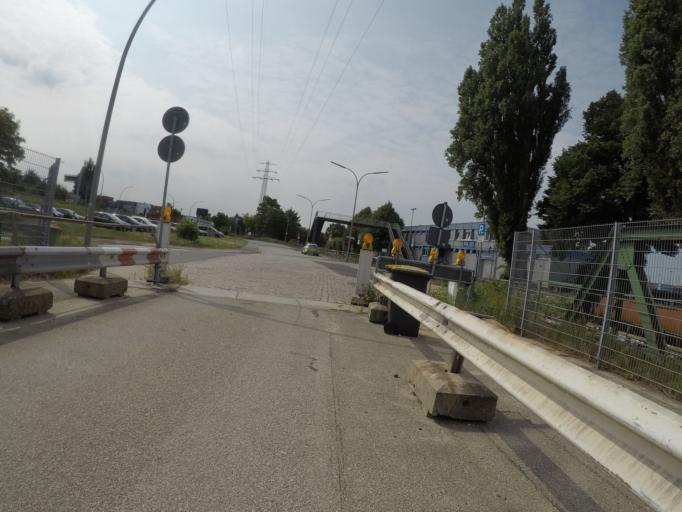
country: DE
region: Hamburg
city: Kleiner Grasbrook
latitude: 53.5257
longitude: 9.9730
